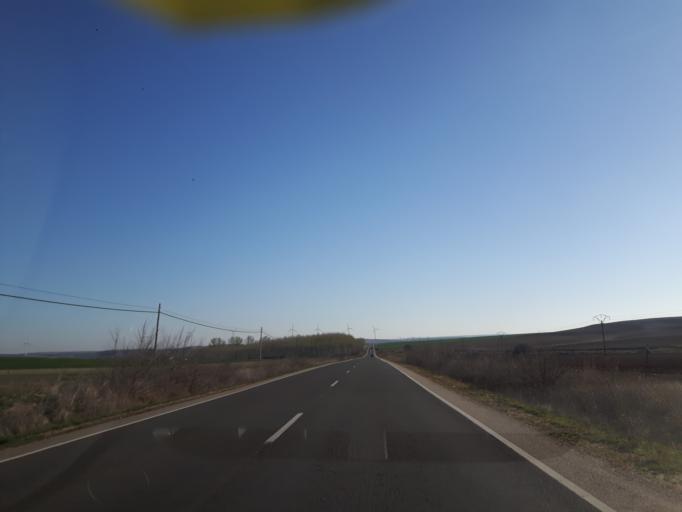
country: ES
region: Castille and Leon
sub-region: Provincia de Salamanca
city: Aldeaseca de Alba
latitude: 40.8424
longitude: -5.4666
